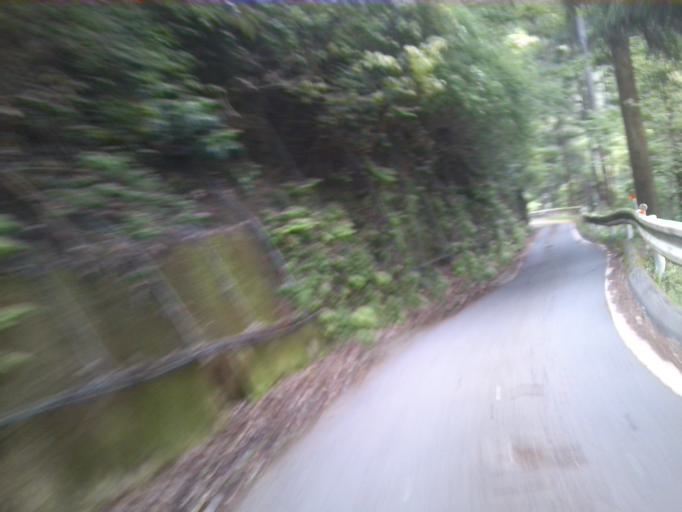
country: JP
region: Kyoto
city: Muko
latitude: 34.9526
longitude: 135.6425
